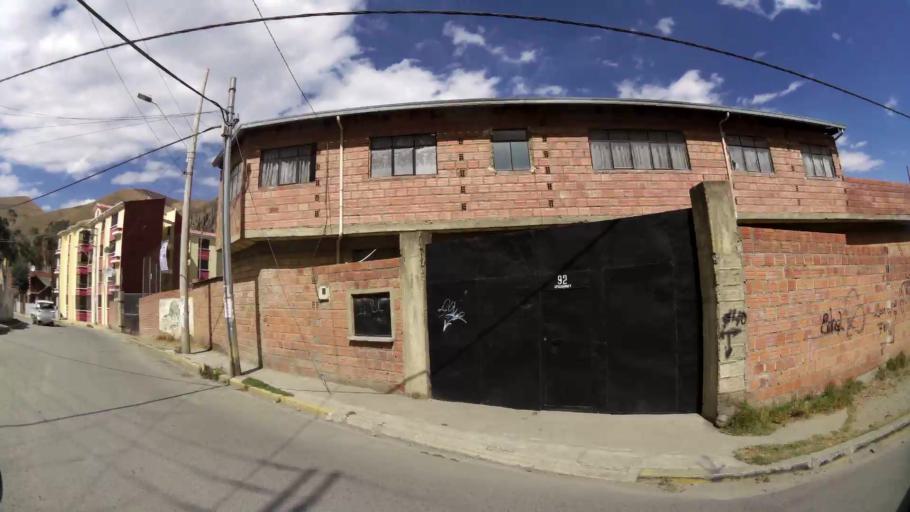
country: BO
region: La Paz
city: La Paz
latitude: -16.4629
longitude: -68.1073
